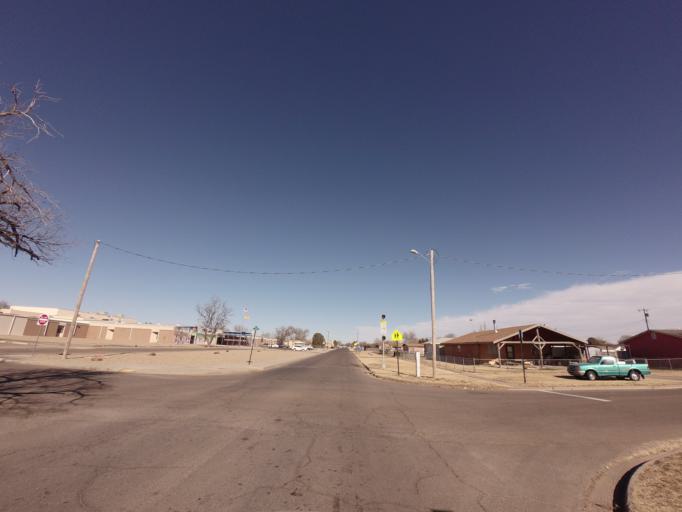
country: US
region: New Mexico
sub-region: Curry County
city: Clovis
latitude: 34.4017
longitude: -103.2167
